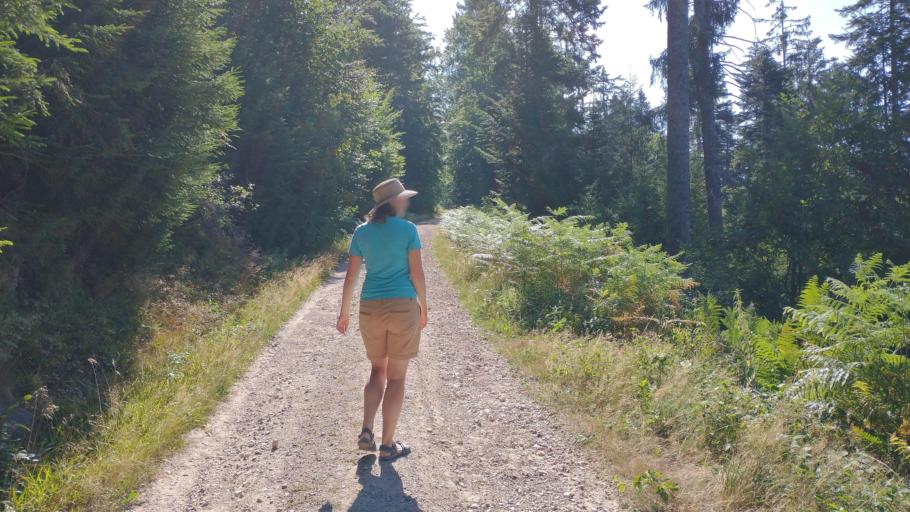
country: DE
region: Baden-Wuerttemberg
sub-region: Freiburg Region
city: Nordrach
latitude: 48.4338
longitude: 8.1108
